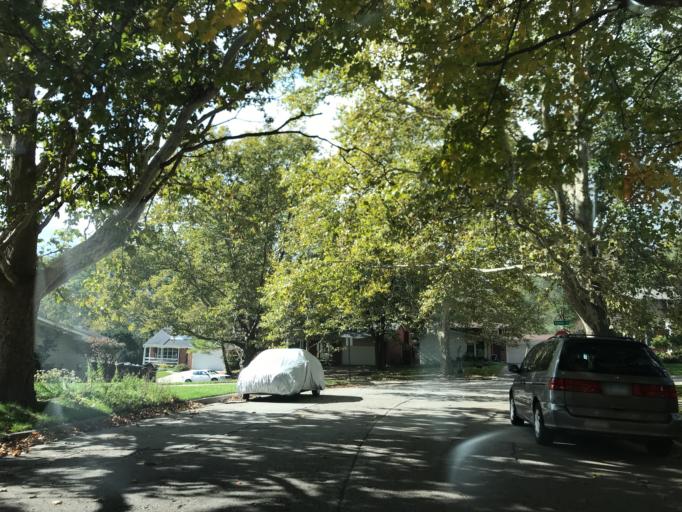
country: US
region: Michigan
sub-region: Washtenaw County
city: Ann Arbor
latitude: 42.2470
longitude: -83.7137
